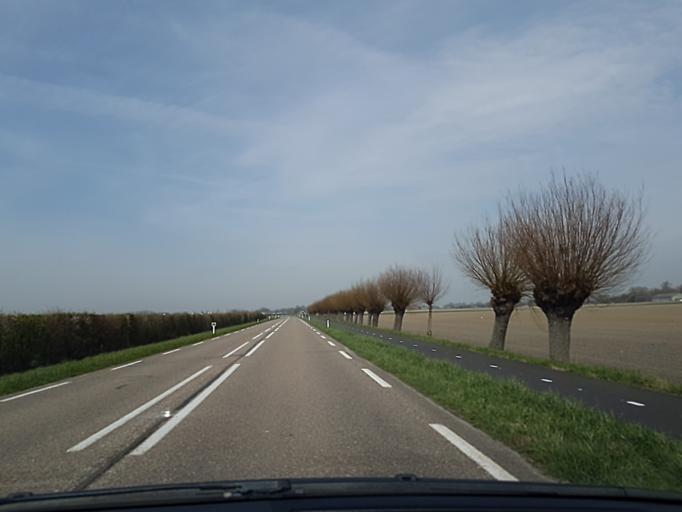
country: NL
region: Zeeland
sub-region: Gemeente Hulst
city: Hulst
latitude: 51.3495
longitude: 4.0303
